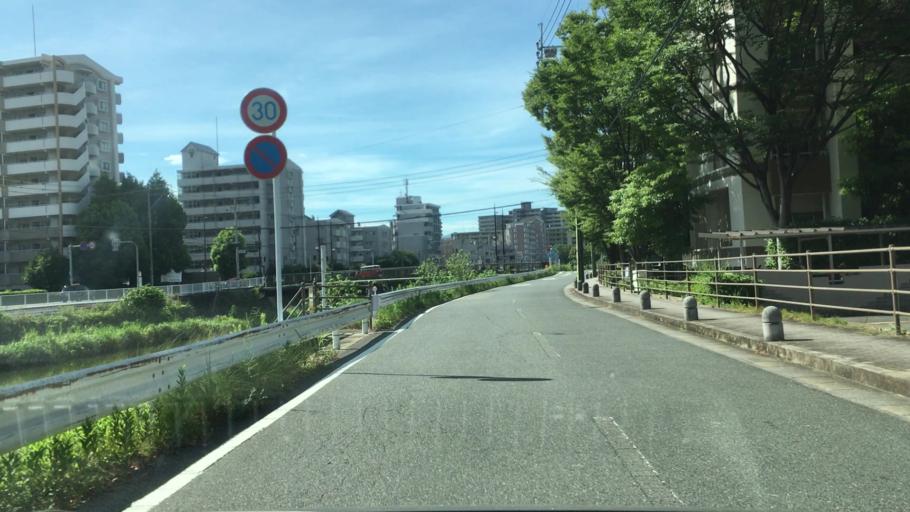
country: JP
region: Fukuoka
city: Fukuoka-shi
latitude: 33.5748
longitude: 130.3751
